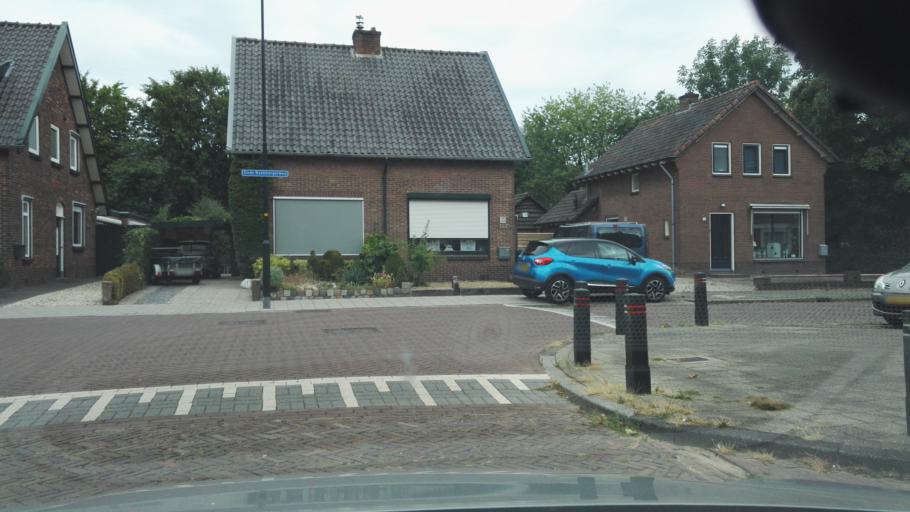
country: NL
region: Gelderland
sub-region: Gemeente Apeldoorn
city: Apeldoorn
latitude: 52.1950
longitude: 5.9698
